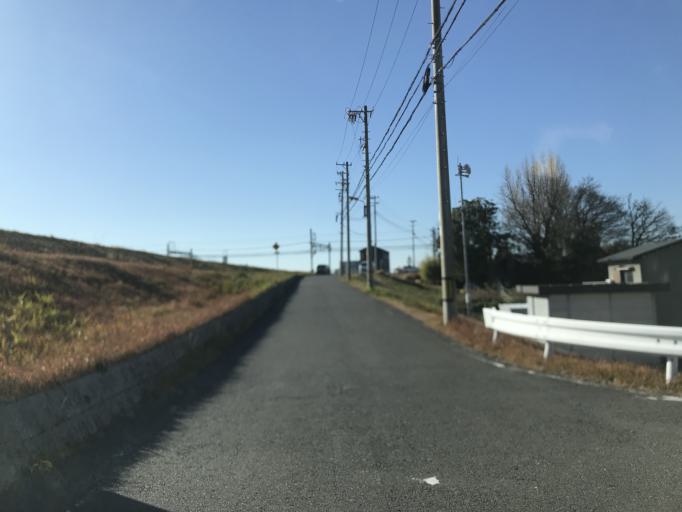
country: JP
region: Aichi
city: Nagoya-shi
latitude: 35.1956
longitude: 136.8694
